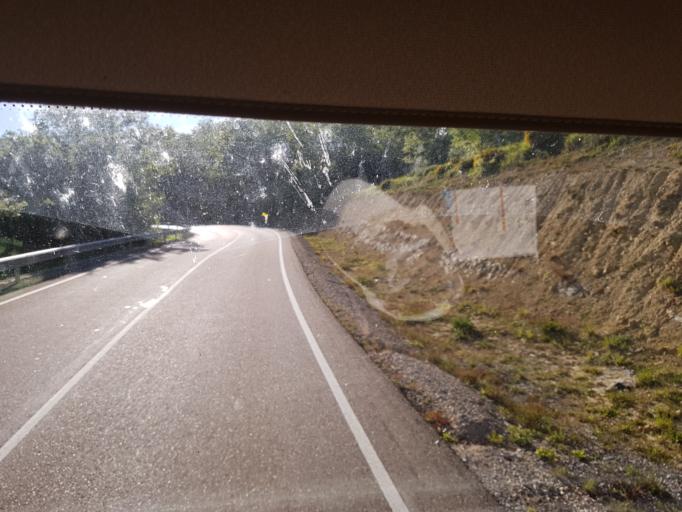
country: ES
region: Cantabria
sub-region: Provincia de Cantabria
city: San Pedro del Romeral
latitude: 42.9903
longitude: -3.7621
